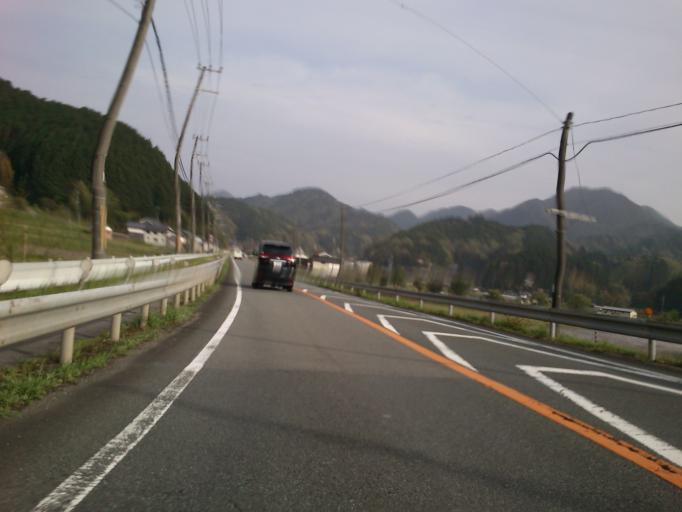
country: JP
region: Hyogo
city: Sasayama
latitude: 35.0841
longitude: 135.3194
